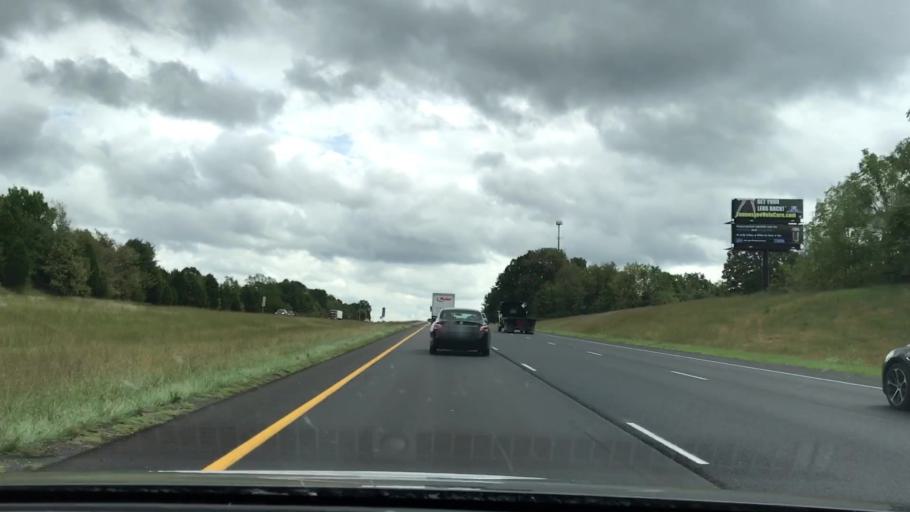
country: US
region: Tennessee
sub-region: Robertson County
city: Coopertown
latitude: 36.3546
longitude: -86.9419
